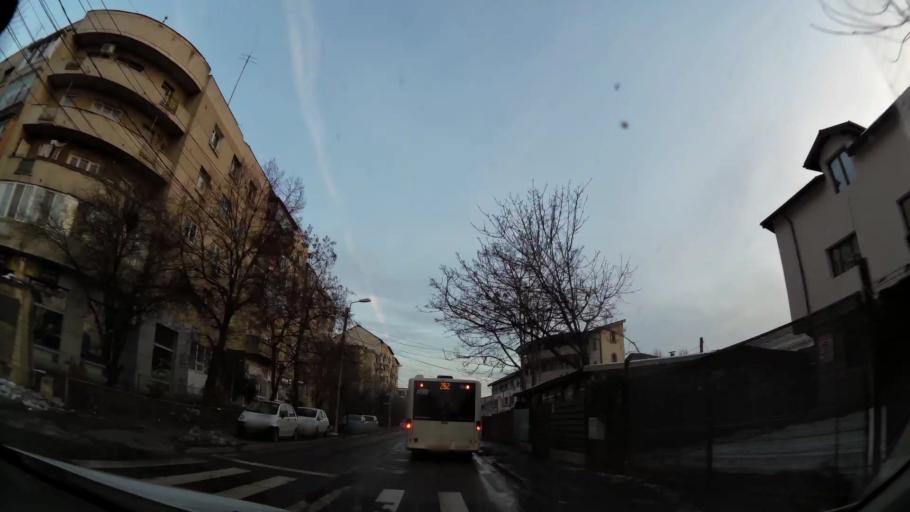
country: RO
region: Ilfov
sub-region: Comuna Fundeni-Dobroesti
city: Fundeni
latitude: 44.4634
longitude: 26.1410
